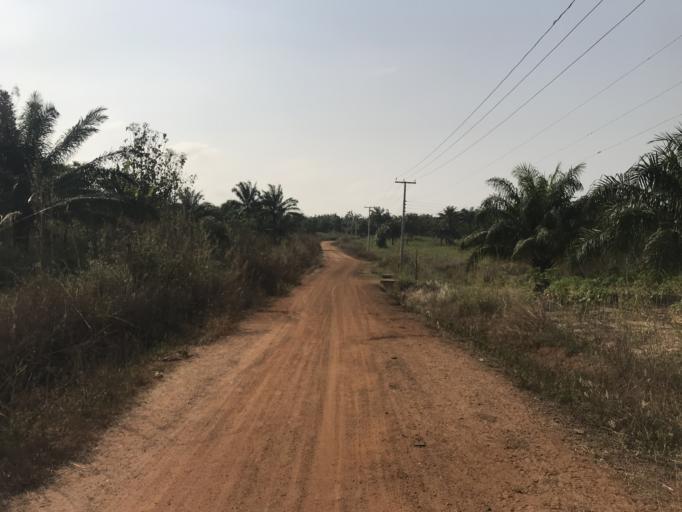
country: NG
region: Osun
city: Olupona
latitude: 7.6108
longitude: 4.1455
